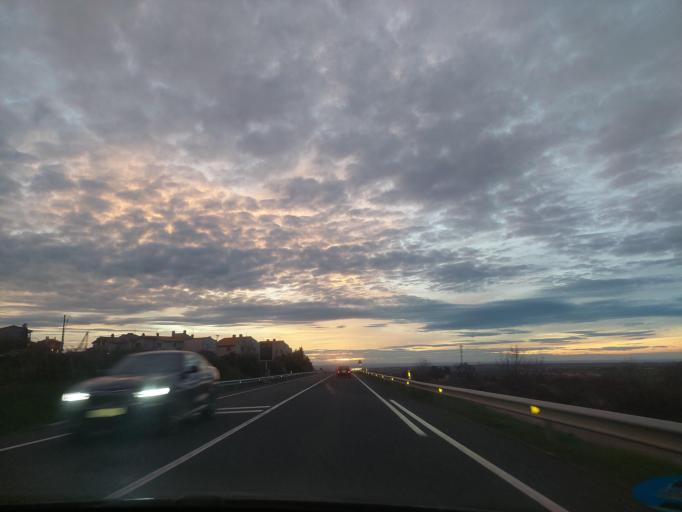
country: ES
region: Castille and Leon
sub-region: Provincia de Segovia
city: Torrecaballeros
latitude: 40.9934
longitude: -4.0261
